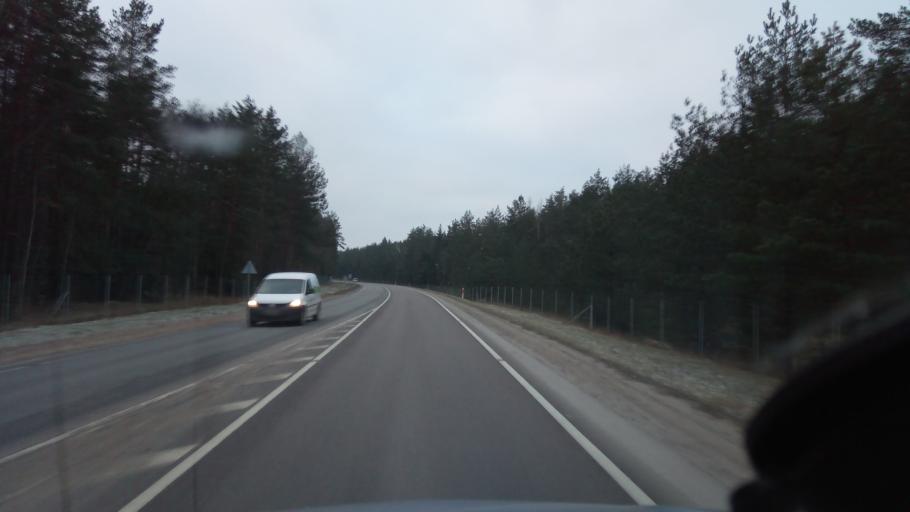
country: LT
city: Trakai
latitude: 54.5310
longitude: 24.9859
